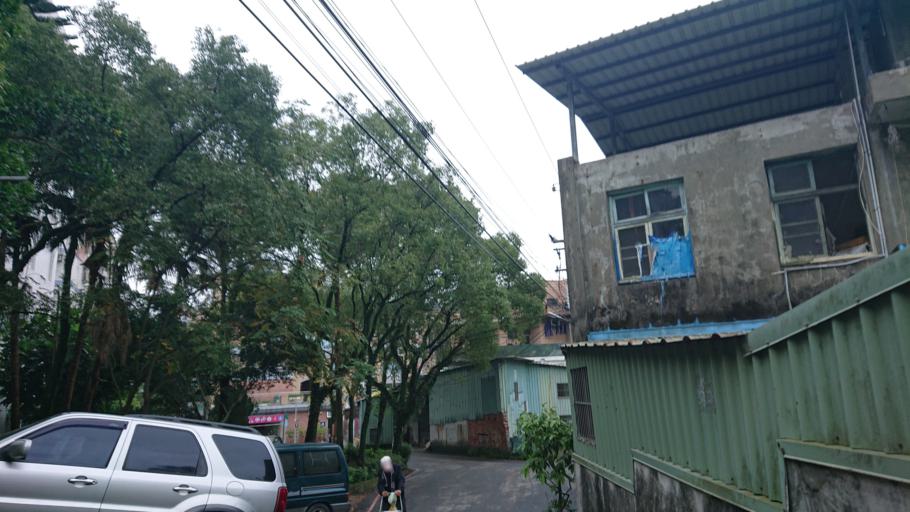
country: TW
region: Taiwan
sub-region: Taoyuan
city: Taoyuan
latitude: 24.9344
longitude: 121.3670
